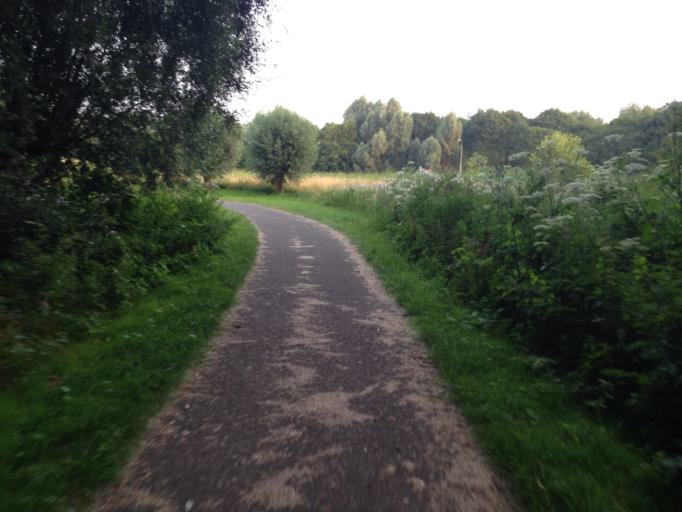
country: NL
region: Flevoland
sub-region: Gemeente Almere
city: Almere Stad
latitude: 52.4082
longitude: 5.2309
